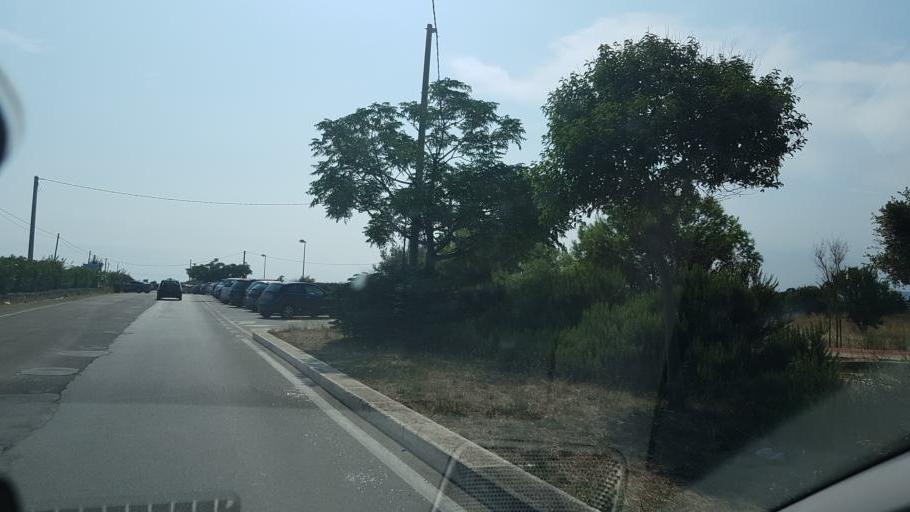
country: IT
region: Apulia
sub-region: Provincia di Bari
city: Monopoli
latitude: 40.9384
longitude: 17.3171
